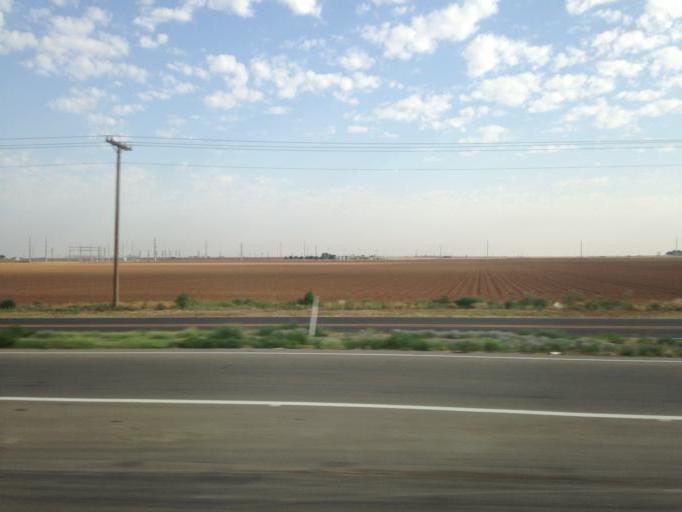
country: US
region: Texas
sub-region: Martin County
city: Stanton
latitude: 32.1031
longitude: -101.8615
